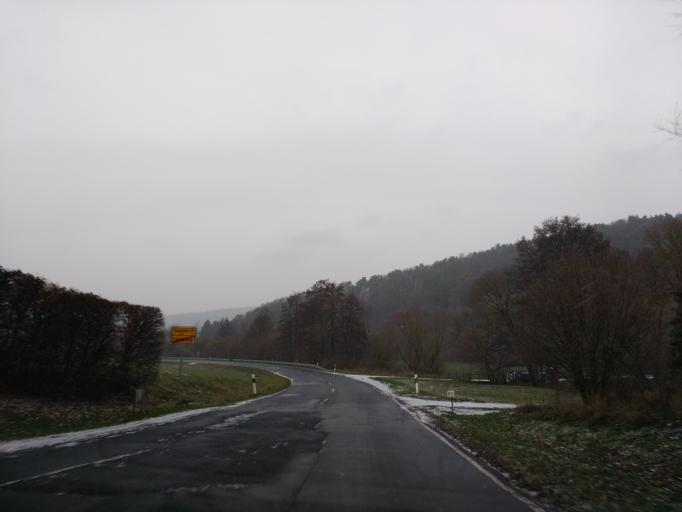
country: DE
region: Hesse
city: Spangenberg
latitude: 51.0982
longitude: 9.7076
